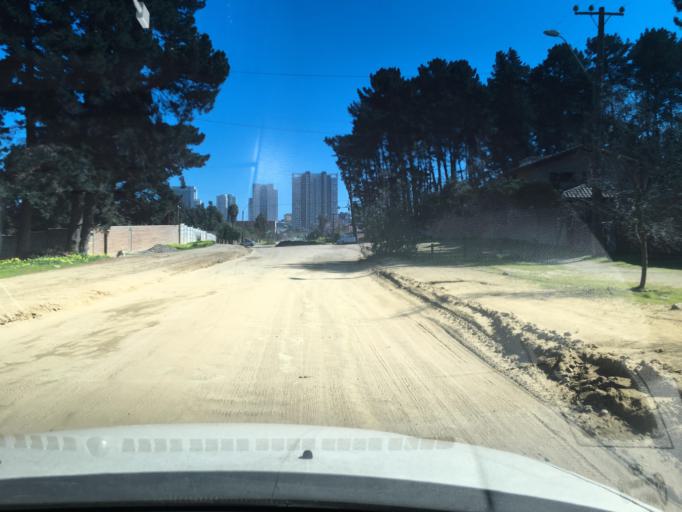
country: CL
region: Valparaiso
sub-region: Provincia de Valparaiso
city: Vina del Mar
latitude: -32.9594
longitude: -71.5352
